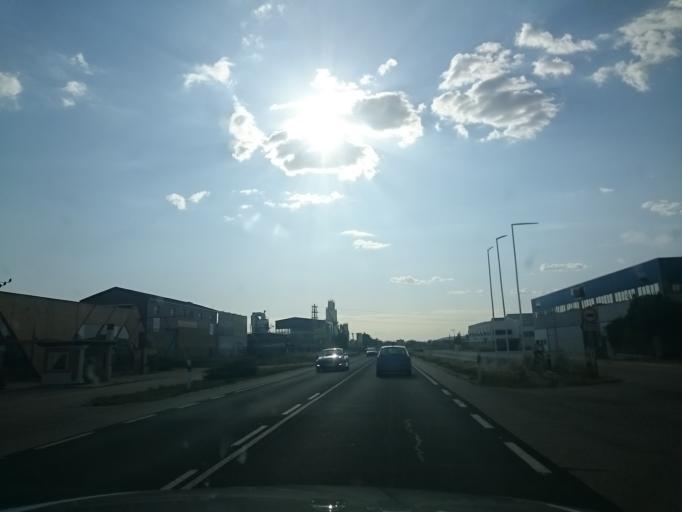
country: ES
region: Castille and Leon
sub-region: Provincia de Burgos
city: Cardenajimeno
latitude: 42.3424
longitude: -3.6176
